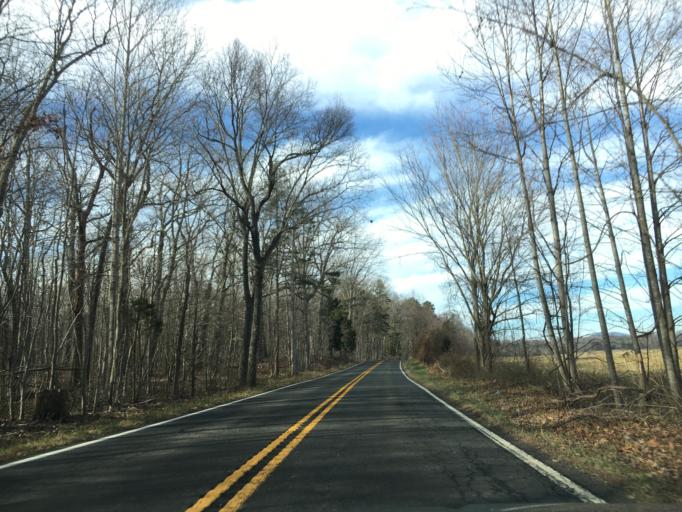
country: US
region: Virginia
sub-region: Fauquier County
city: Warrenton
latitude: 38.7320
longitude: -77.9507
